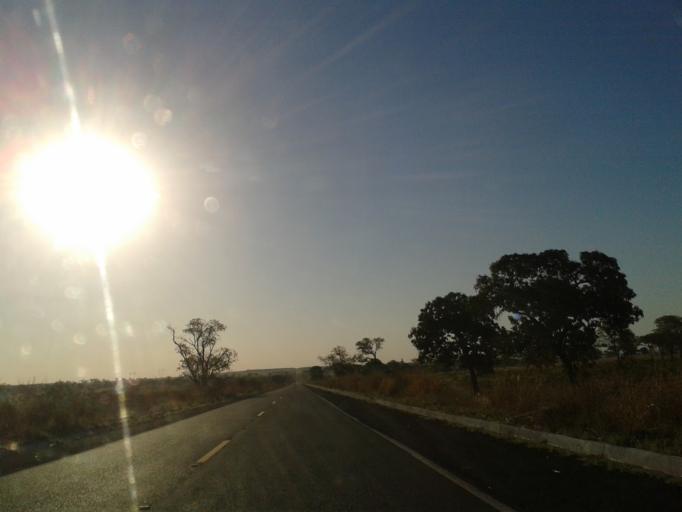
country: BR
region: Minas Gerais
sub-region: Santa Vitoria
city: Santa Vitoria
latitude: -19.0865
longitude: -50.3511
